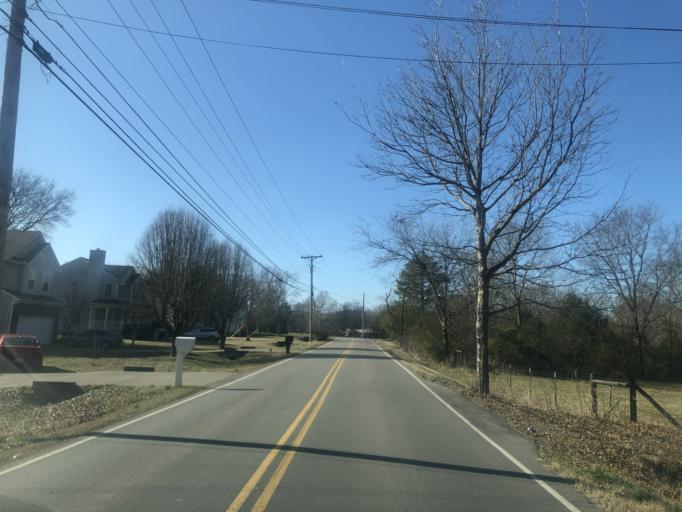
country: US
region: Tennessee
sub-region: Rutherford County
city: Smyrna
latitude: 35.9642
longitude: -86.5325
